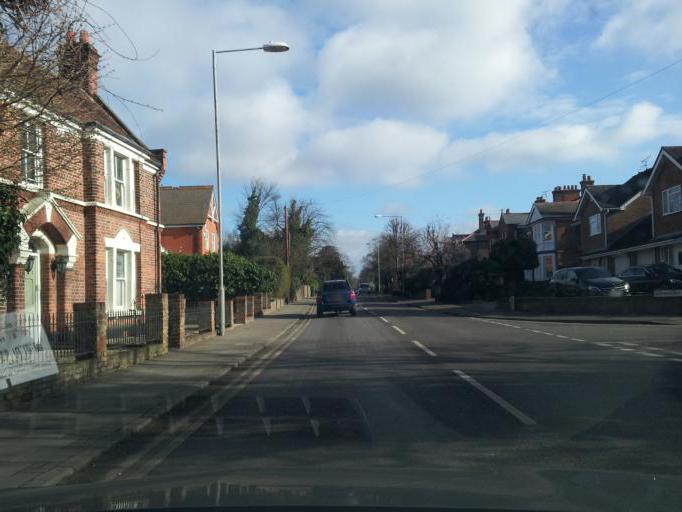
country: GB
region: England
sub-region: Essex
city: Chelmsford
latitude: 51.7386
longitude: 0.4870
